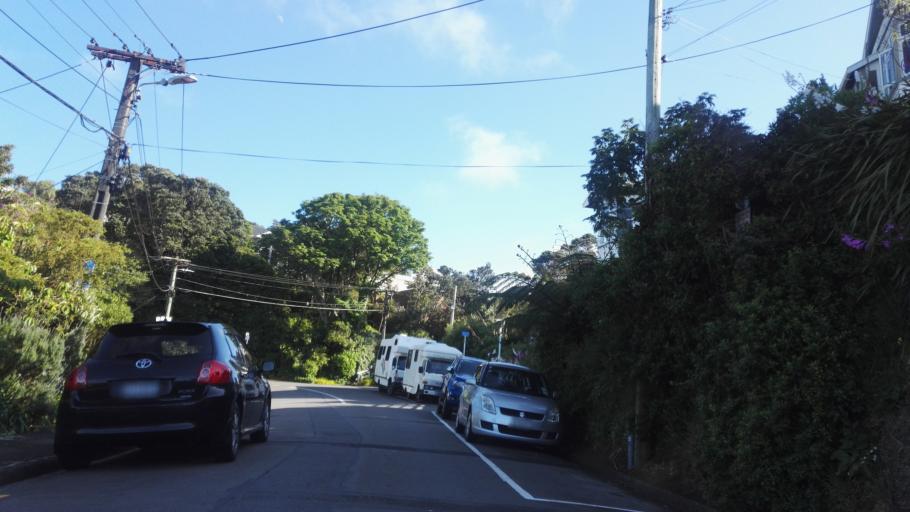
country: NZ
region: Wellington
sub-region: Wellington City
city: Kelburn
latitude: -41.2908
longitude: 174.7638
